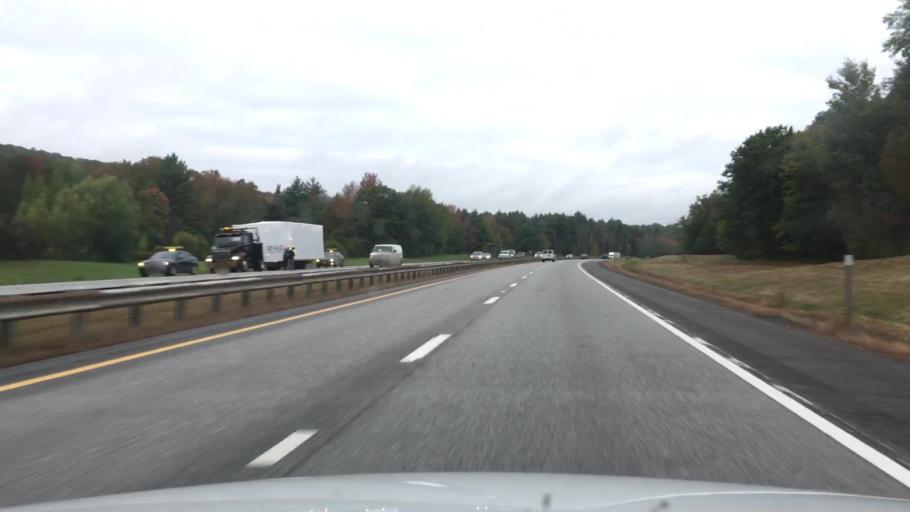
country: US
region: Maine
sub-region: Cumberland County
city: Cumberland Center
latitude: 43.7611
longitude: -70.3092
